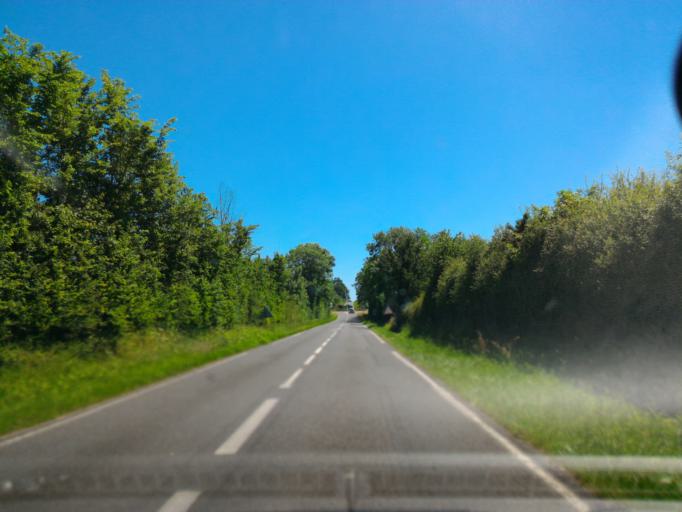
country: FR
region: Poitou-Charentes
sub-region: Departement de la Vienne
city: Availles-Limouzine
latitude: 46.1890
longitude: 0.7239
